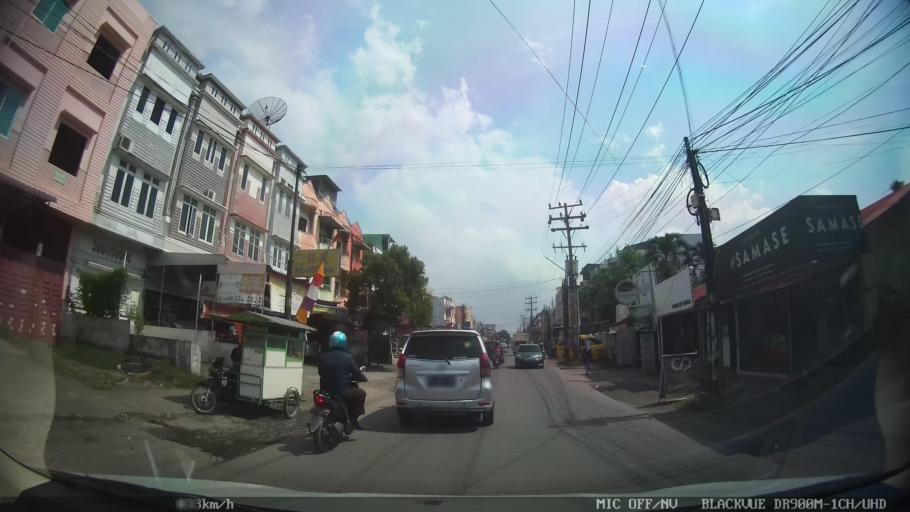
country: ID
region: North Sumatra
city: Medan
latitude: 3.6135
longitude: 98.6656
